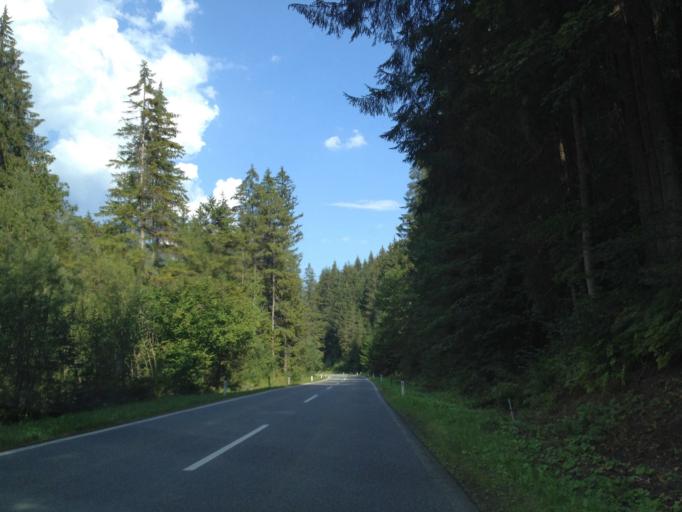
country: AT
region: Styria
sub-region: Politischer Bezirk Liezen
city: Haus
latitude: 47.4197
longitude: 13.7431
